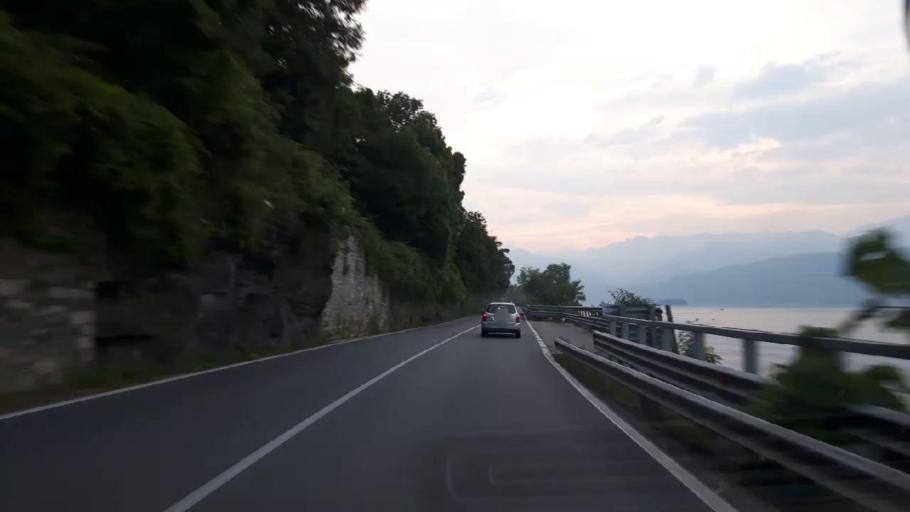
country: IT
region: Piedmont
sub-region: Provincia Verbano-Cusio-Ossola
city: Stresa
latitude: 45.8739
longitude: 8.5613
